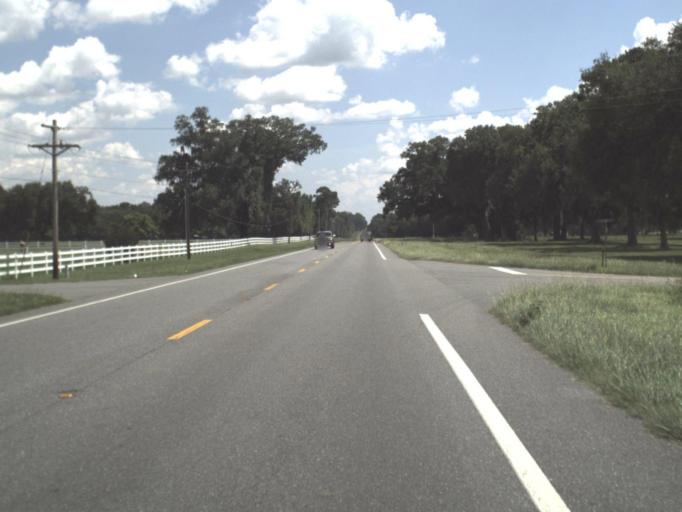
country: US
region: Florida
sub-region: Columbia County
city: Watertown
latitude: 30.0806
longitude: -82.6012
